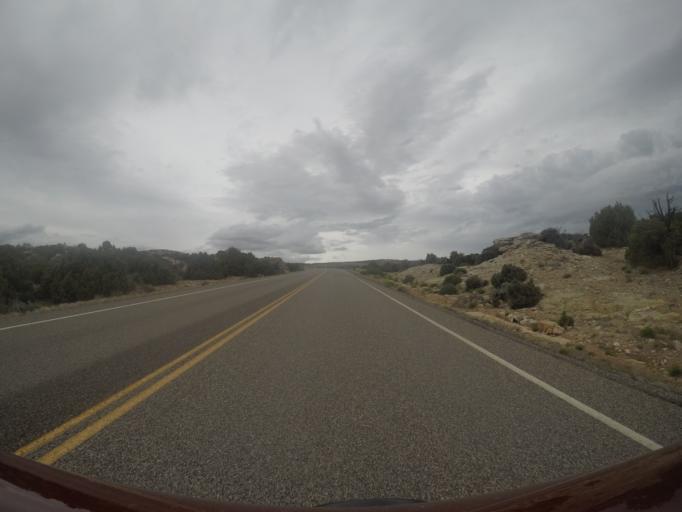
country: US
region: Wyoming
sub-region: Big Horn County
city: Lovell
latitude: 44.9947
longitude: -108.2610
